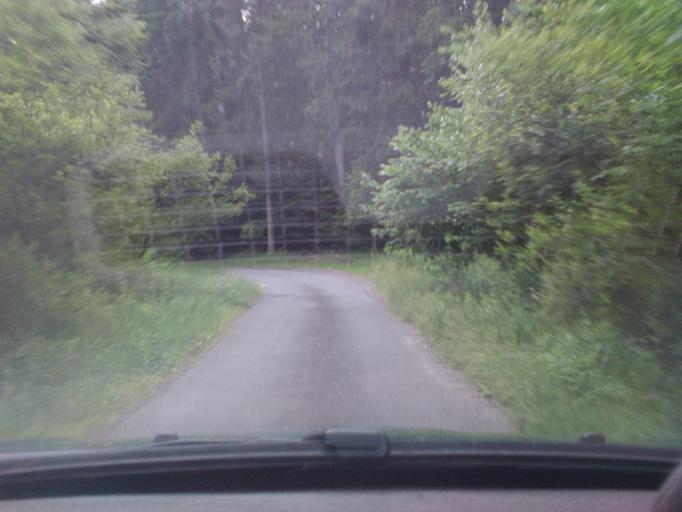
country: FR
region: Lorraine
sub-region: Departement des Vosges
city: Taintrux
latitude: 48.2371
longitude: 6.8147
